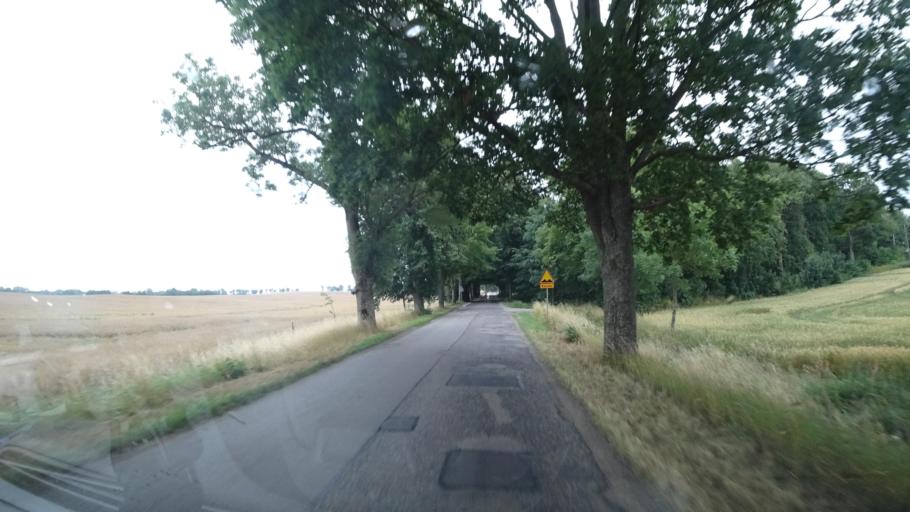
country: PL
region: Warmian-Masurian Voivodeship
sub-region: Powiat gizycki
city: Ryn
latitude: 53.9107
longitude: 21.5603
